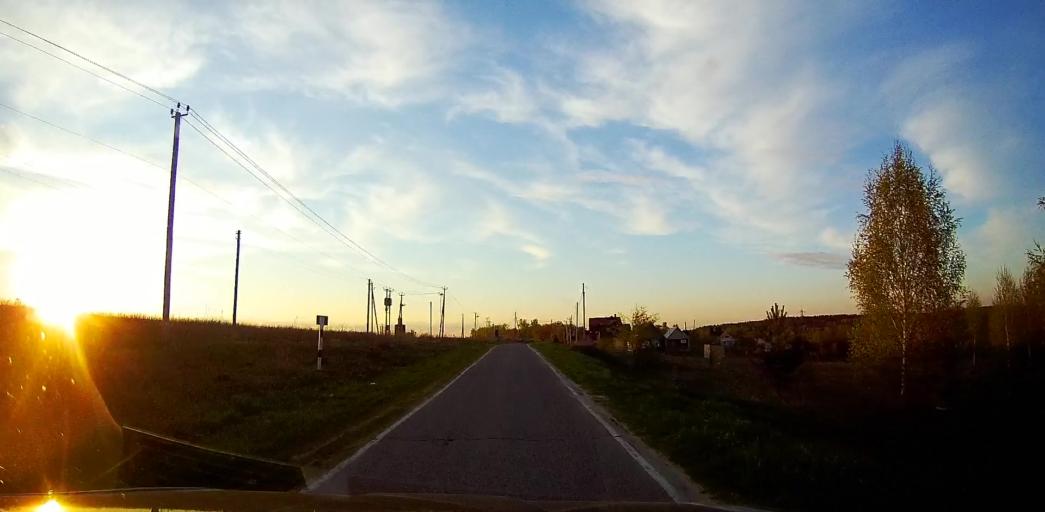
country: RU
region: Moskovskaya
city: Peski
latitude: 55.2266
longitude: 38.7347
